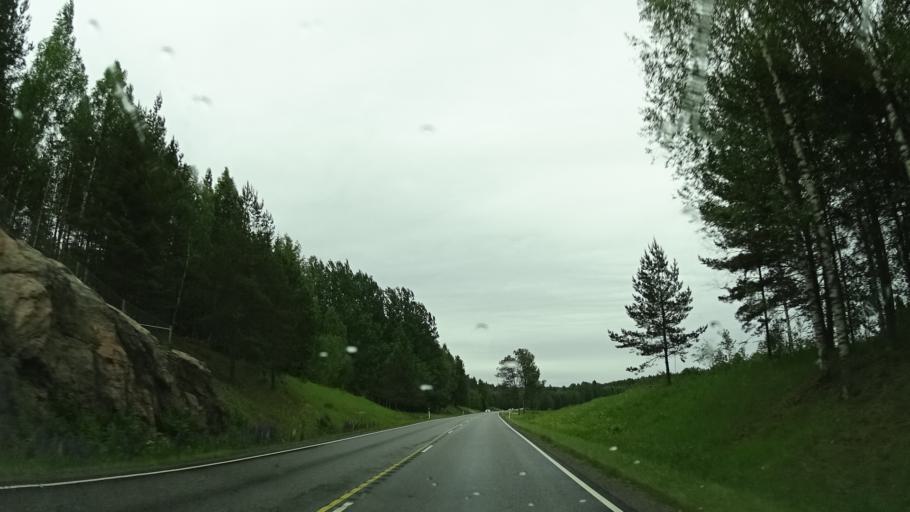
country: FI
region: Varsinais-Suomi
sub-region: Salo
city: Pernioe
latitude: 60.0808
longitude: 23.2428
